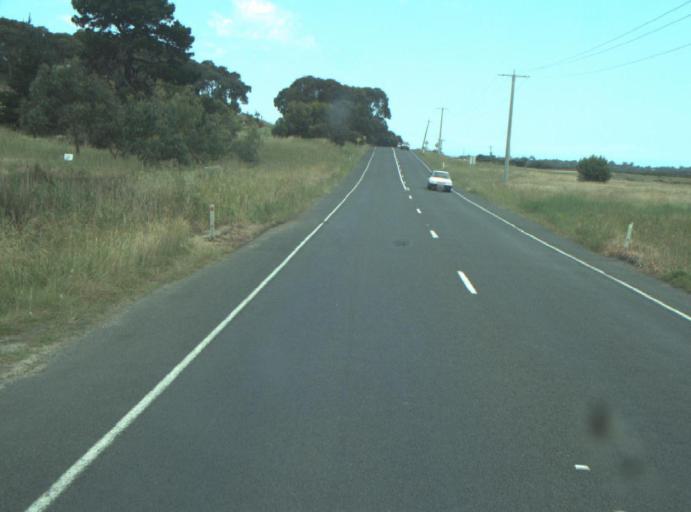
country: AU
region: Victoria
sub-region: Greater Geelong
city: Leopold
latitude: -38.2467
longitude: 144.5048
